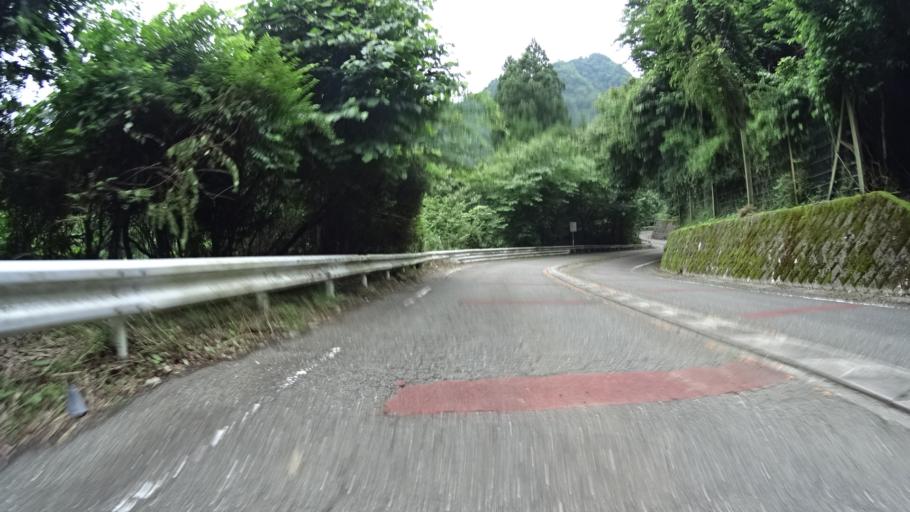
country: JP
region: Kanagawa
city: Hadano
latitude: 35.5019
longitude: 139.2309
